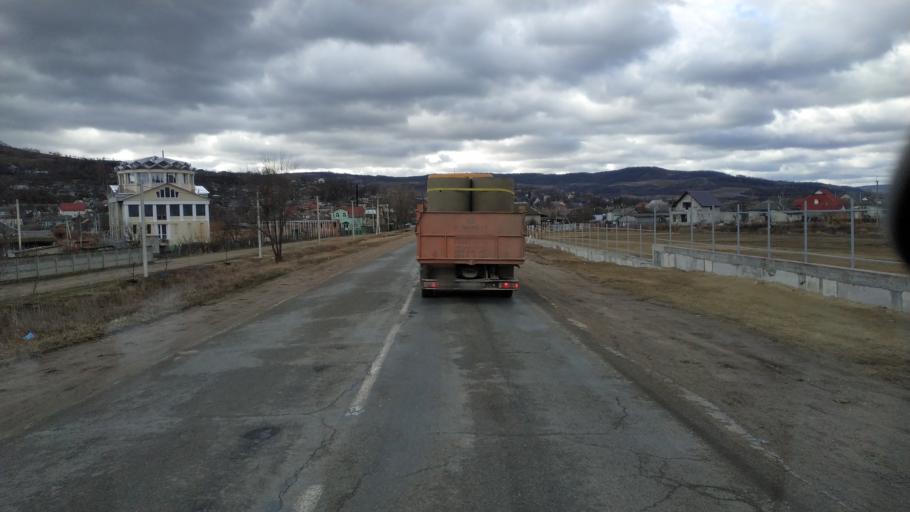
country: MD
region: Stinga Nistrului
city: Bucovat
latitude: 47.1621
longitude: 28.4348
